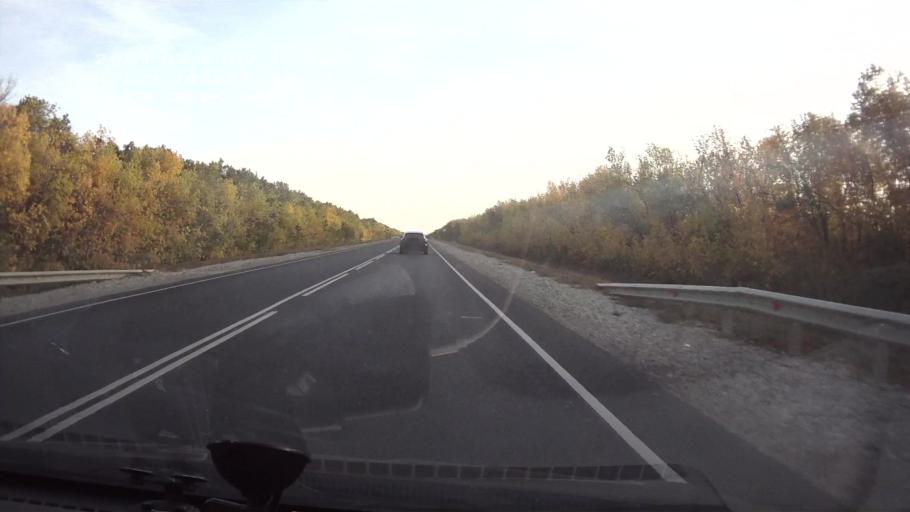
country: RU
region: Saratov
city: Krasnoarmeysk
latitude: 51.0946
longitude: 45.6479
